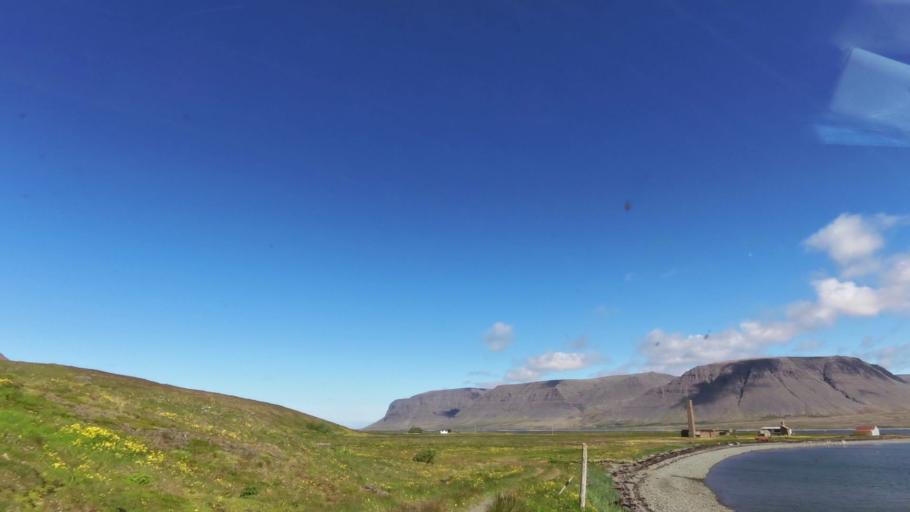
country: IS
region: West
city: Olafsvik
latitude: 65.6373
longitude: -23.9325
